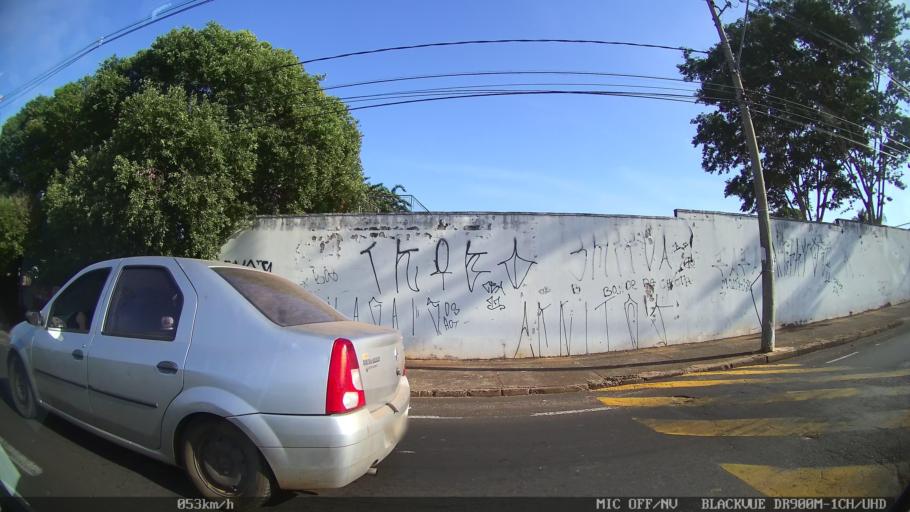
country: BR
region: Sao Paulo
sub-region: Sao Jose Do Rio Preto
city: Sao Jose do Rio Preto
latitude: -20.7842
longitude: -49.4084
